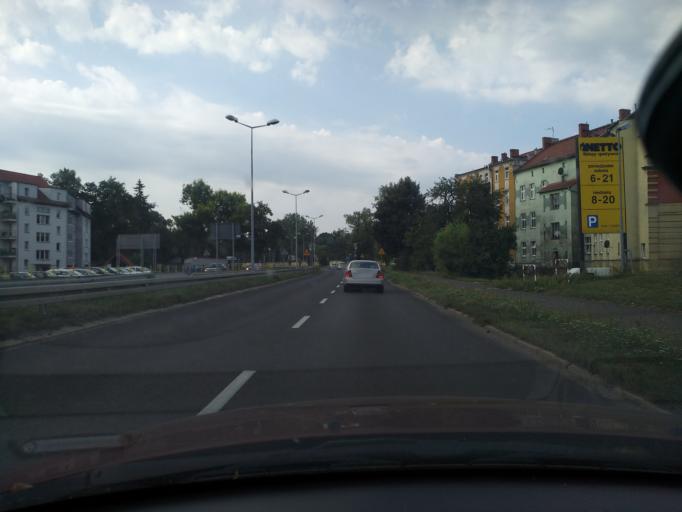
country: PL
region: Lower Silesian Voivodeship
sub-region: Powiat lubanski
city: Luban
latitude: 51.1173
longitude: 15.2940
